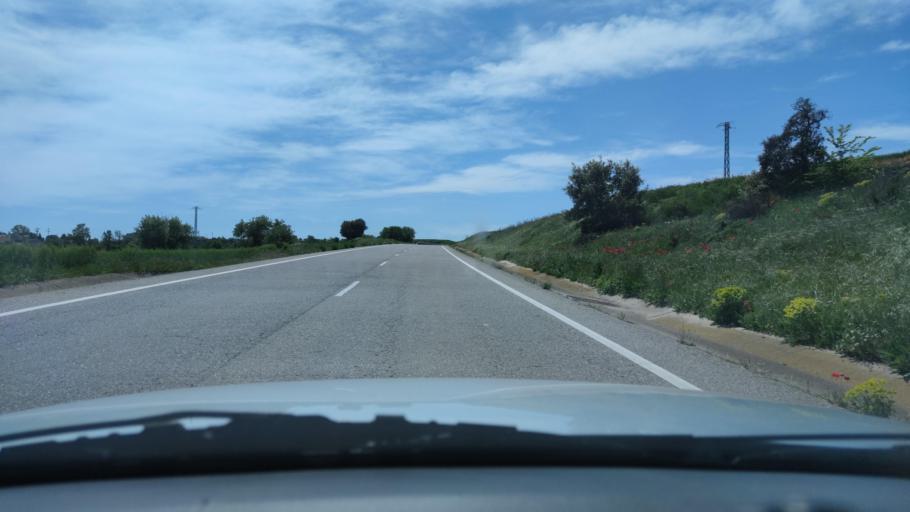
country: ES
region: Catalonia
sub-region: Provincia de Lleida
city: Tora de Riubregos
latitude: 41.8035
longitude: 1.3093
